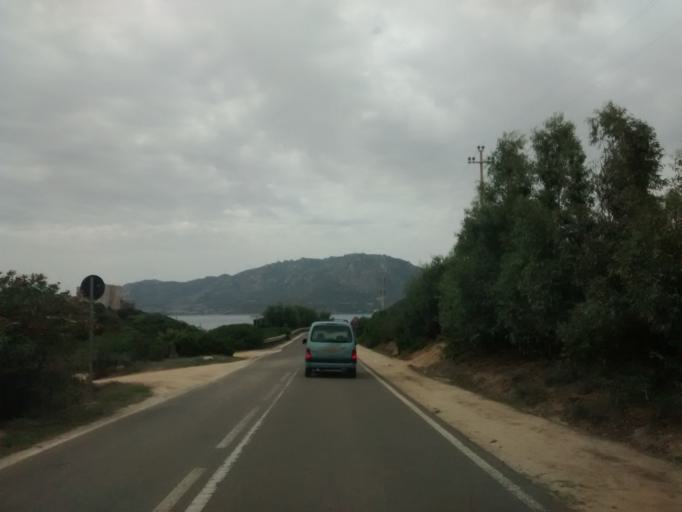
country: IT
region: Sardinia
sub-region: Provincia di Cagliari
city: Villasimius
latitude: 39.1151
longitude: 9.5070
